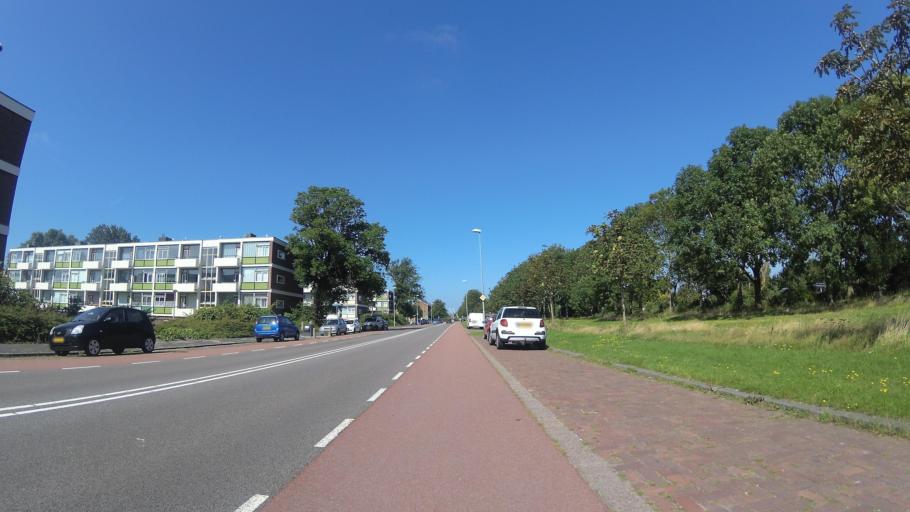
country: NL
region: North Holland
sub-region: Gemeente Den Helder
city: Den Helder
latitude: 52.9428
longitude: 4.7497
